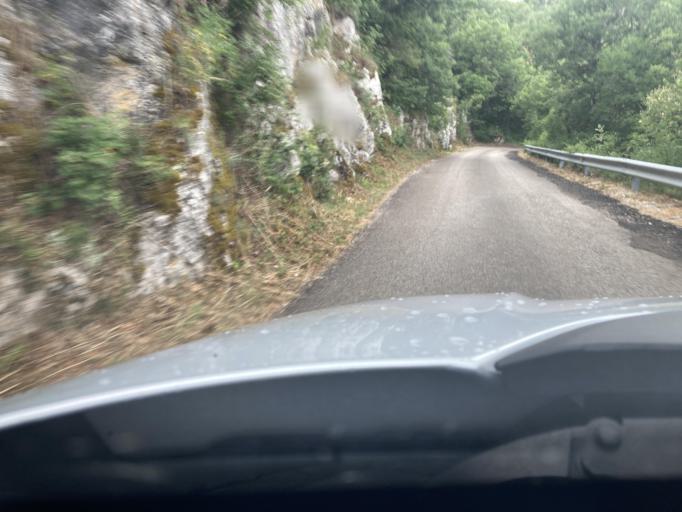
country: IT
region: Abruzzo
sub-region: Provincia dell' Aquila
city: Fossa
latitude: 42.2848
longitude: 13.4939
